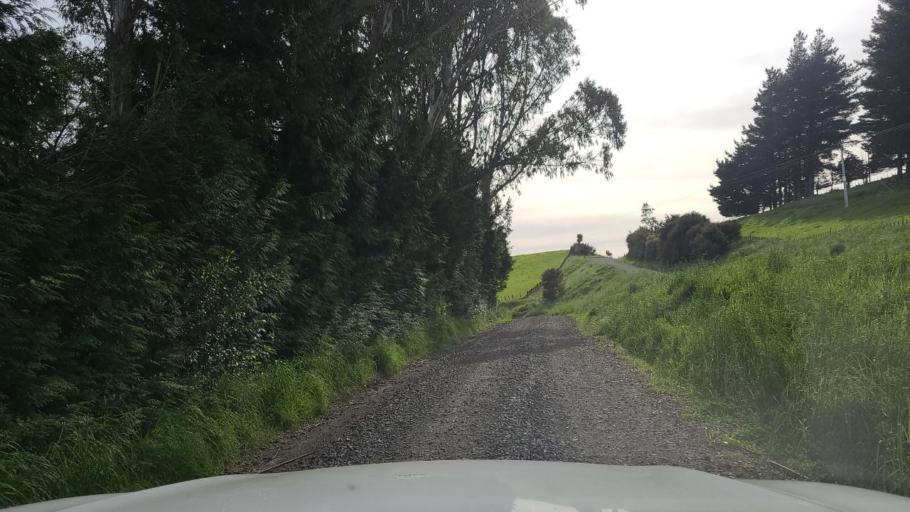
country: NZ
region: Hawke's Bay
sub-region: Napier City
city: Taradale
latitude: -39.3009
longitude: 176.6385
